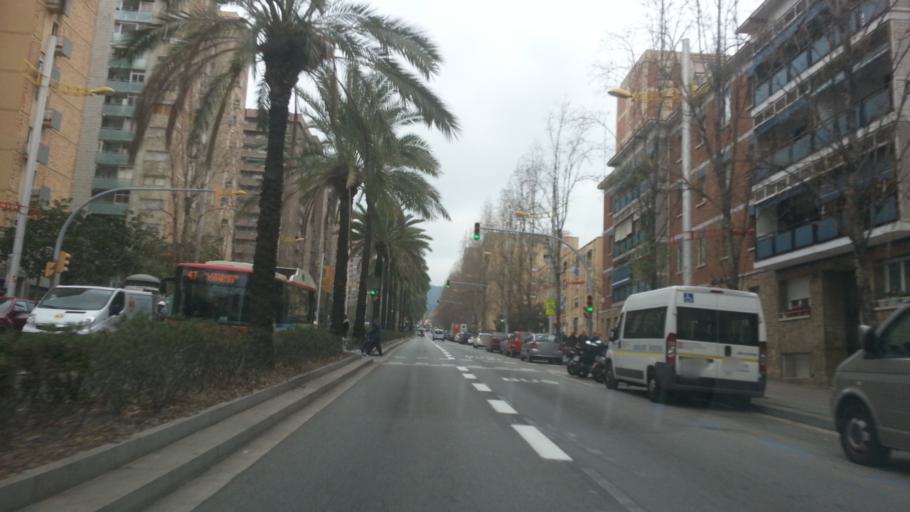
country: ES
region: Catalonia
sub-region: Provincia de Barcelona
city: Nou Barris
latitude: 41.4389
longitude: 2.1688
